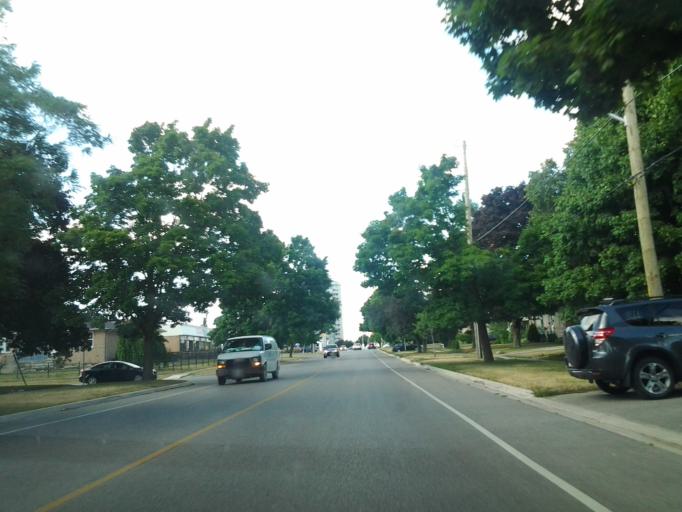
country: CA
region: Ontario
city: Brampton
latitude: 43.6471
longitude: -79.8809
